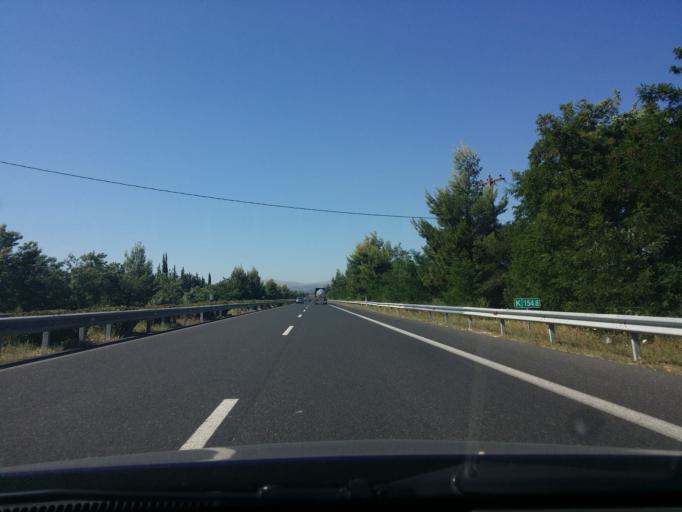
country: GR
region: Peloponnese
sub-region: Nomos Arkadias
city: Tripoli
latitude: 37.5340
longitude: 22.4127
